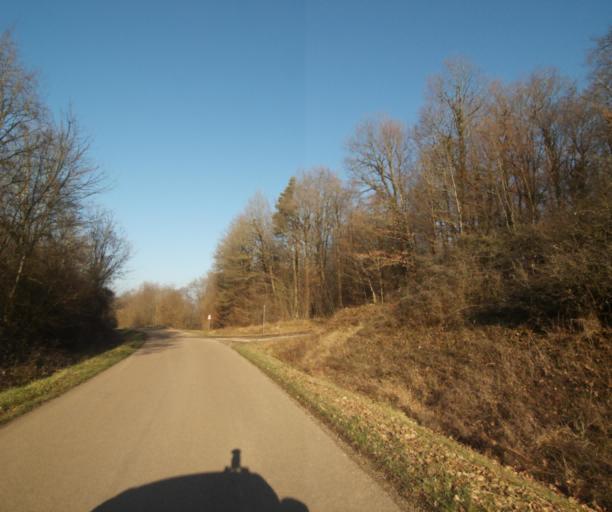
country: FR
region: Champagne-Ardenne
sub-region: Departement de la Haute-Marne
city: Chevillon
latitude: 48.5176
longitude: 5.0919
